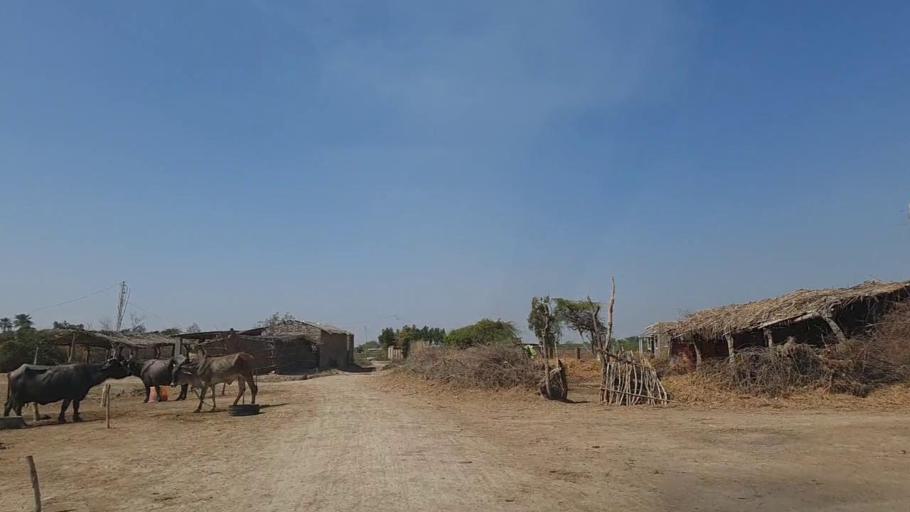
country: PK
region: Sindh
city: Pithoro
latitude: 25.4063
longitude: 69.3081
